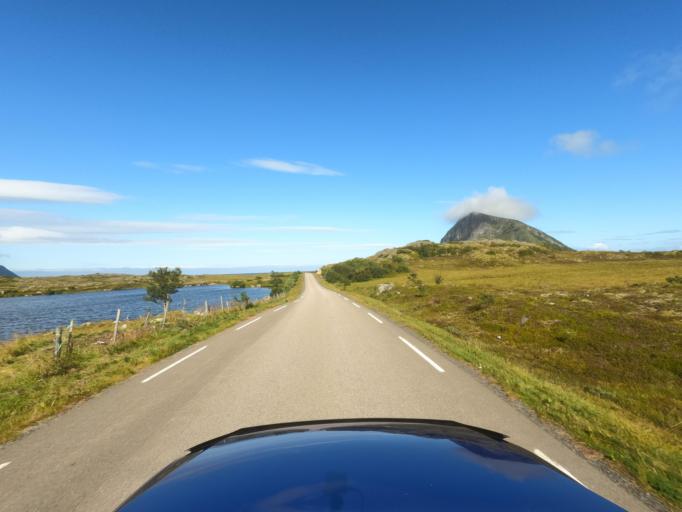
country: NO
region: Nordland
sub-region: Vestvagoy
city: Evjen
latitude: 68.3100
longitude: 14.0966
